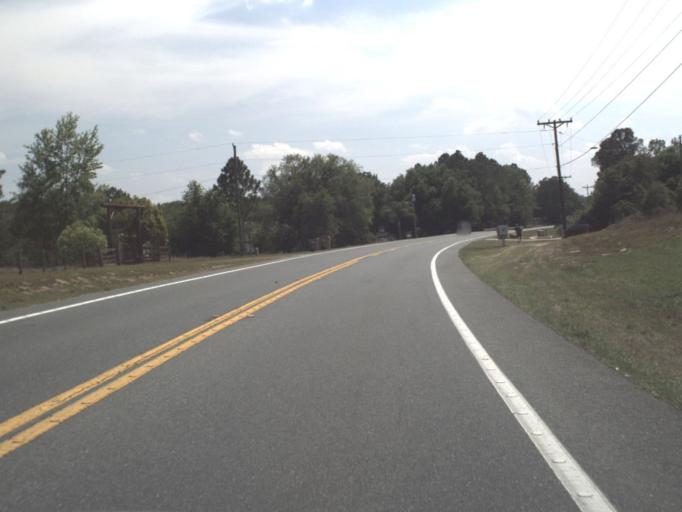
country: US
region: Florida
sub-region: Lake County
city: Howie In The Hills
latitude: 28.6785
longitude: -81.7787
